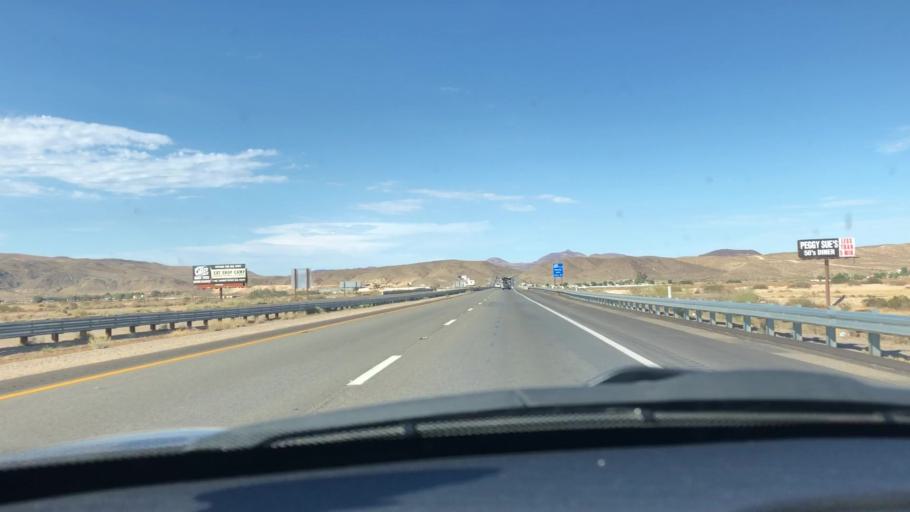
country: US
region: California
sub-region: San Bernardino County
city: Barstow
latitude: 34.8938
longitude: -116.9975
